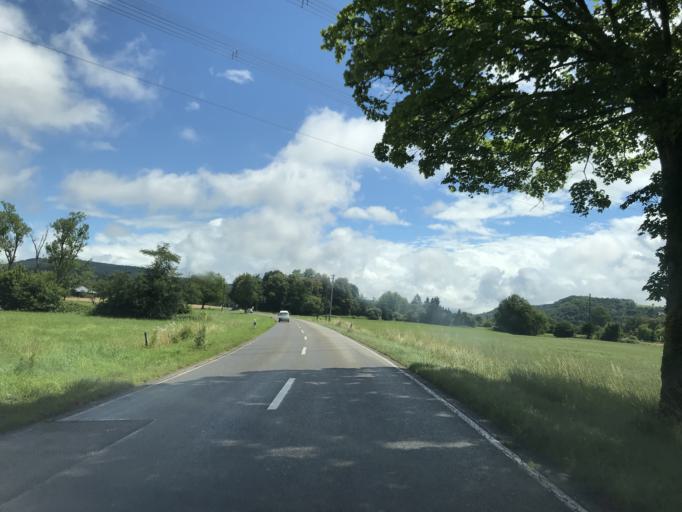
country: DE
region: Baden-Wuerttemberg
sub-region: Freiburg Region
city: Steinen
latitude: 47.6401
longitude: 7.7188
